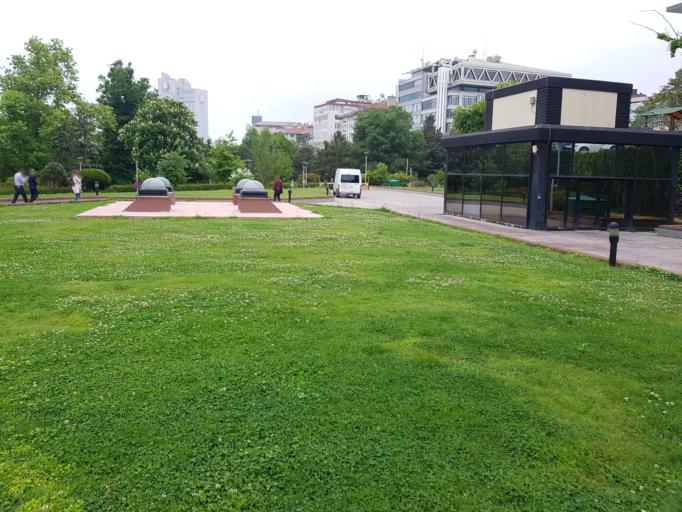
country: TR
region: Istanbul
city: Sisli
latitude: 41.0444
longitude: 28.9879
